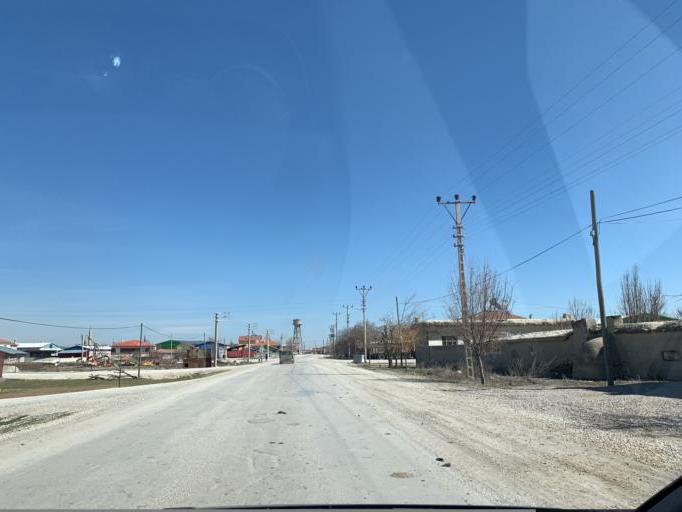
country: TR
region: Konya
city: Yarma
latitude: 37.7507
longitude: 32.8550
